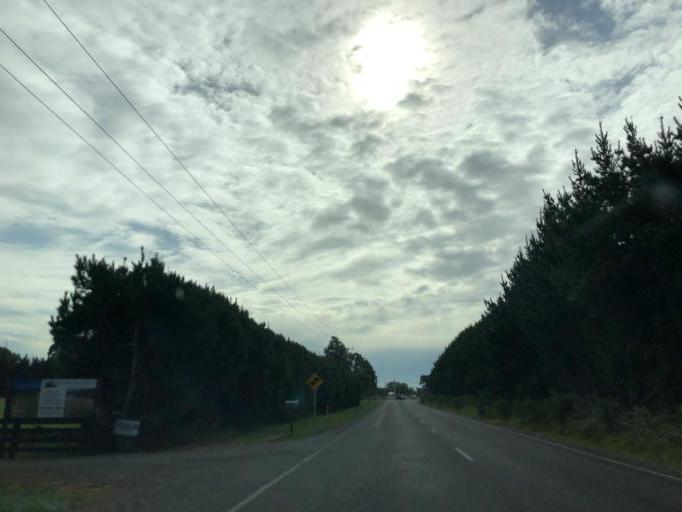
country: NZ
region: Canterbury
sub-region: Selwyn District
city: Rolleston
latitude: -43.6237
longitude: 172.4094
